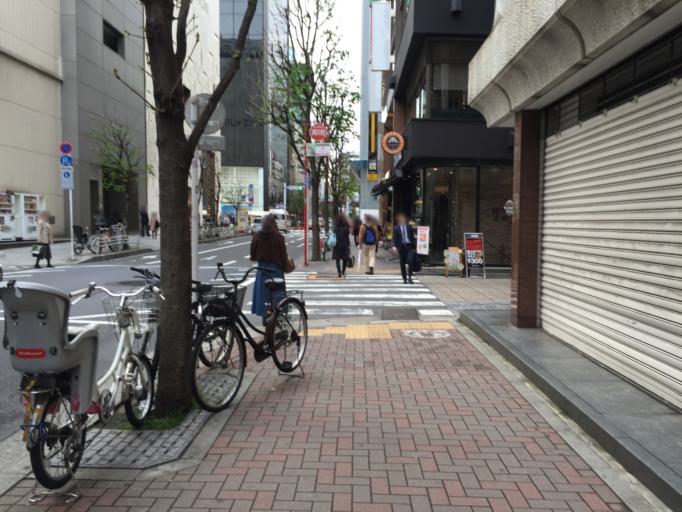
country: JP
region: Tokyo
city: Tokyo
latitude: 35.6726
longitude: 139.7675
